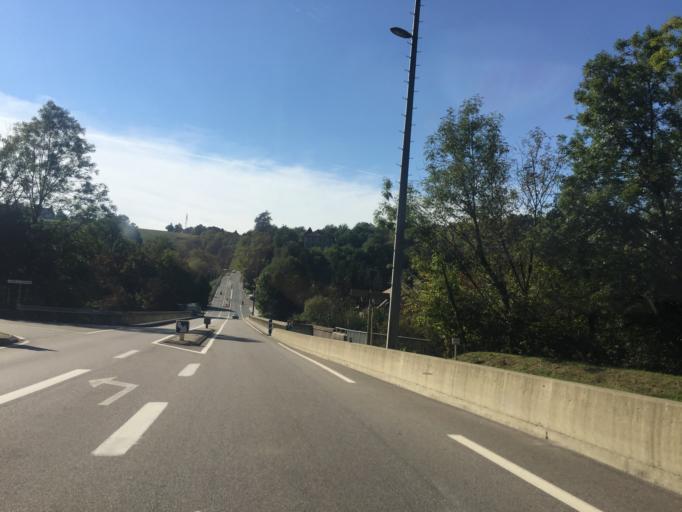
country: FR
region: Rhone-Alpes
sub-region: Departement de la Haute-Savoie
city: Alby-sur-Cheran
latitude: 45.8201
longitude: 6.0266
